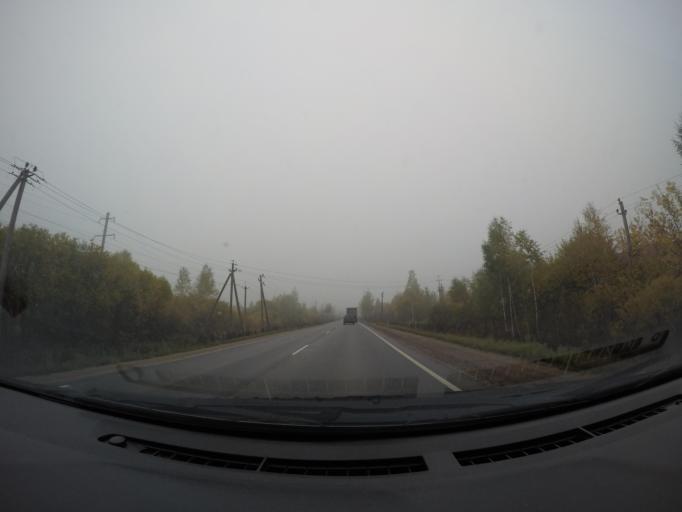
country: RU
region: Moskovskaya
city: Rumyantsevo
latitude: 55.8759
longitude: 36.5725
